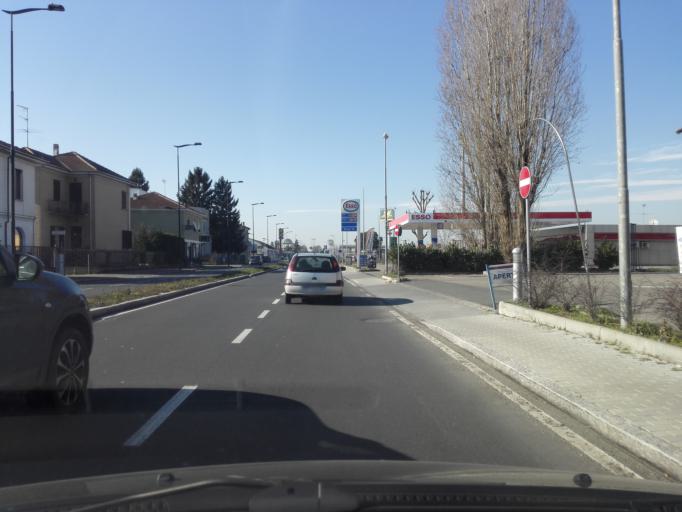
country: IT
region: Piedmont
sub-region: Provincia di Alessandria
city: Alessandria
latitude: 44.9188
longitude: 8.5972
